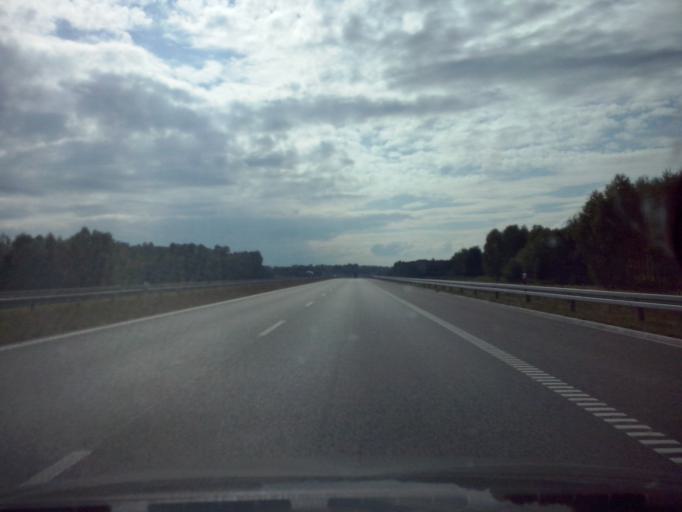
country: PL
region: Lesser Poland Voivodeship
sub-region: Powiat tarnowski
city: Lisia Gora
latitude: 50.0704
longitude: 21.0787
